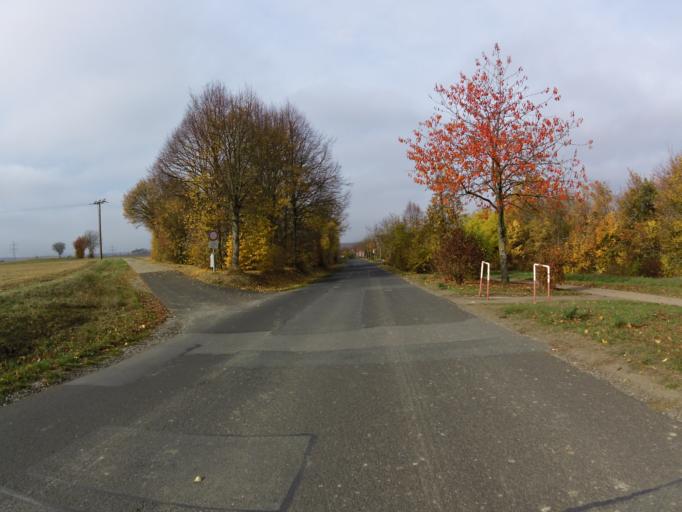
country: DE
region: Bavaria
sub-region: Regierungsbezirk Unterfranken
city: Eisingen
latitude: 49.7565
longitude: 9.8292
